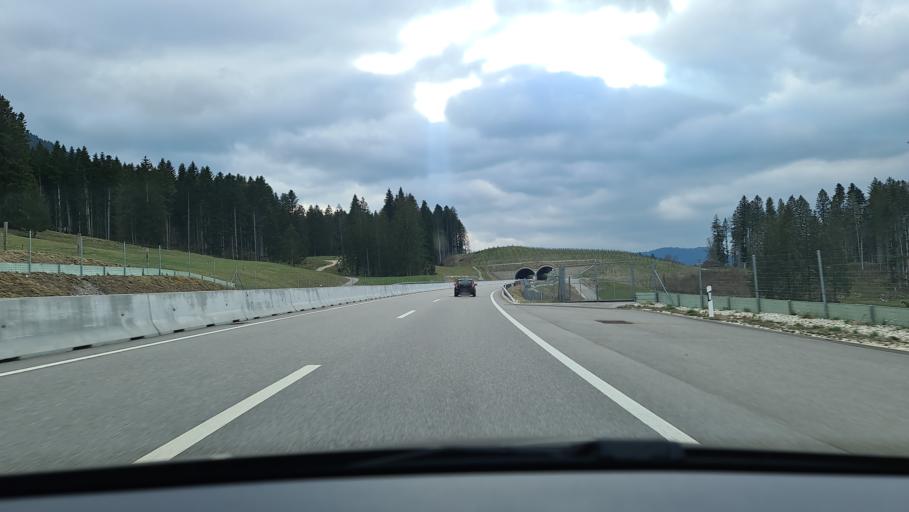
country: CH
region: Bern
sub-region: Jura bernois
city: Bevilard
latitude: 47.2306
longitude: 7.2832
